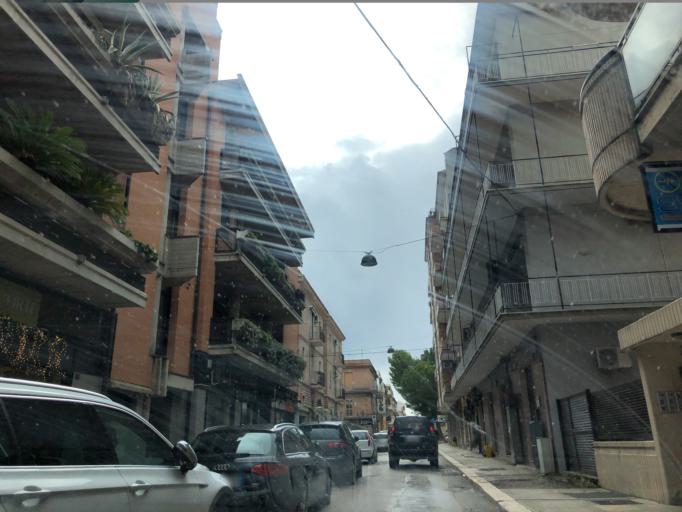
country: IT
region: Apulia
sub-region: Provincia di Foggia
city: Lucera
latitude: 41.5092
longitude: 15.3303
